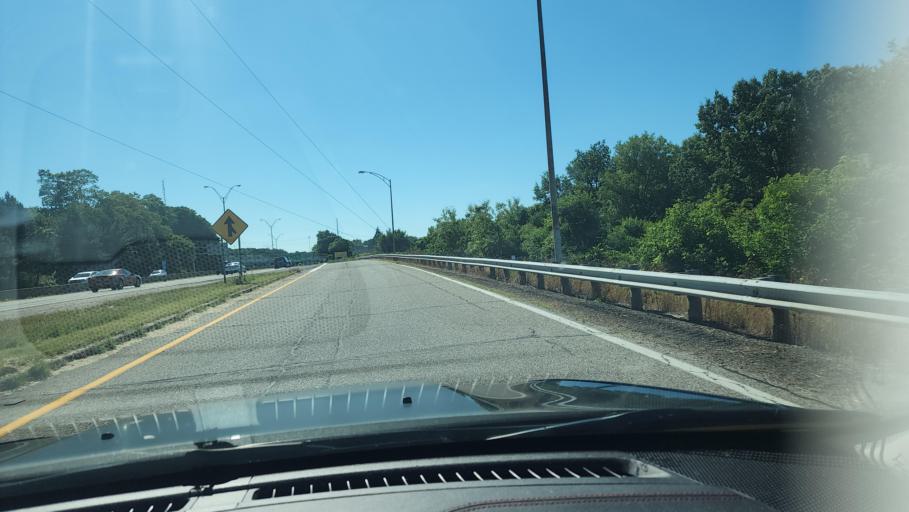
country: US
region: Ohio
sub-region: Mahoning County
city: Youngstown
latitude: 41.0814
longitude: -80.6379
